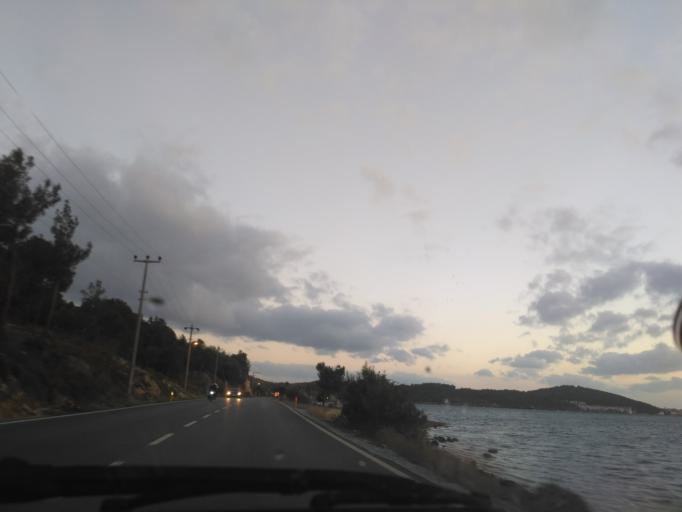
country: TR
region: Balikesir
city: Ayvalik
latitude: 39.2913
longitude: 26.6694
